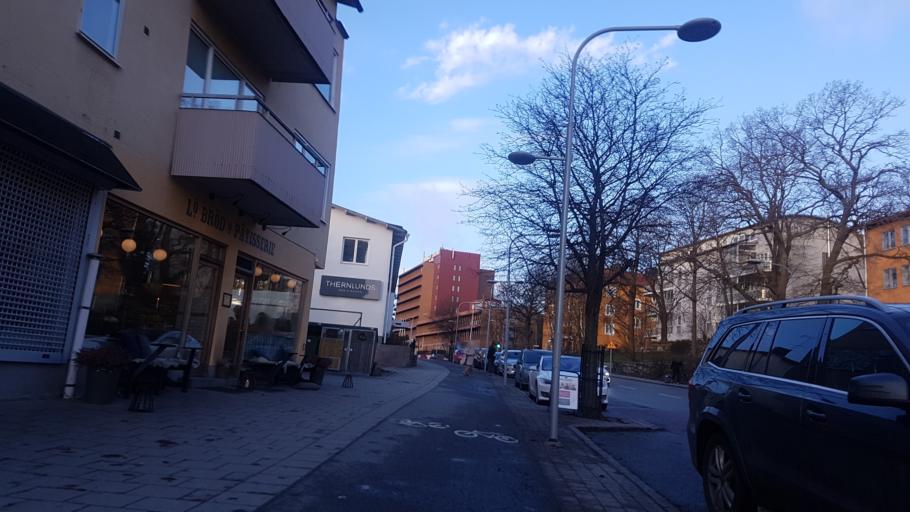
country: SE
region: Stockholm
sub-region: Lidingo
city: Lidingoe
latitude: 59.3650
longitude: 18.1292
